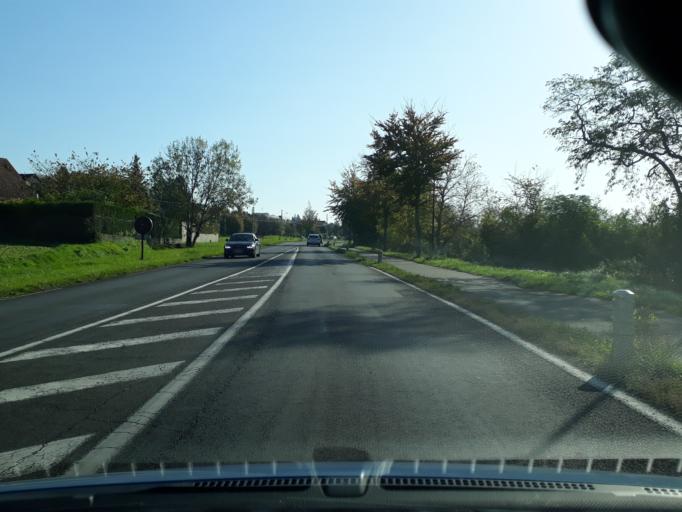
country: FR
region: Ile-de-France
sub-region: Departement de Seine-et-Marne
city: Livry-sur-Seine
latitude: 48.5155
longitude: 2.6742
